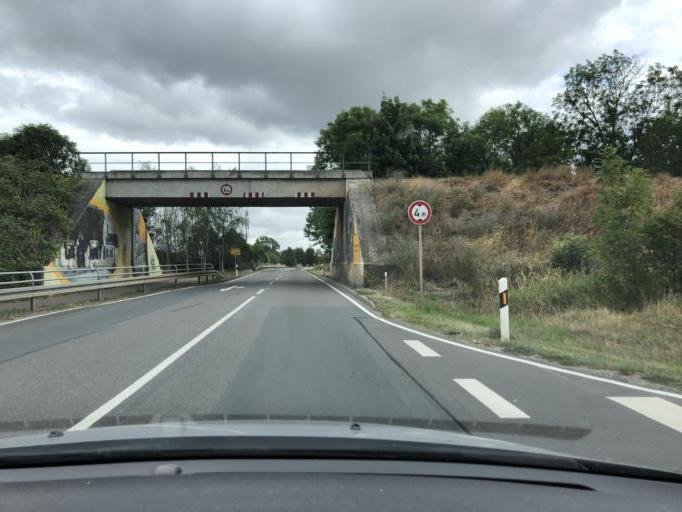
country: DE
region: Saxony-Anhalt
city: Lochau
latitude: 51.4013
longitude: 12.0427
